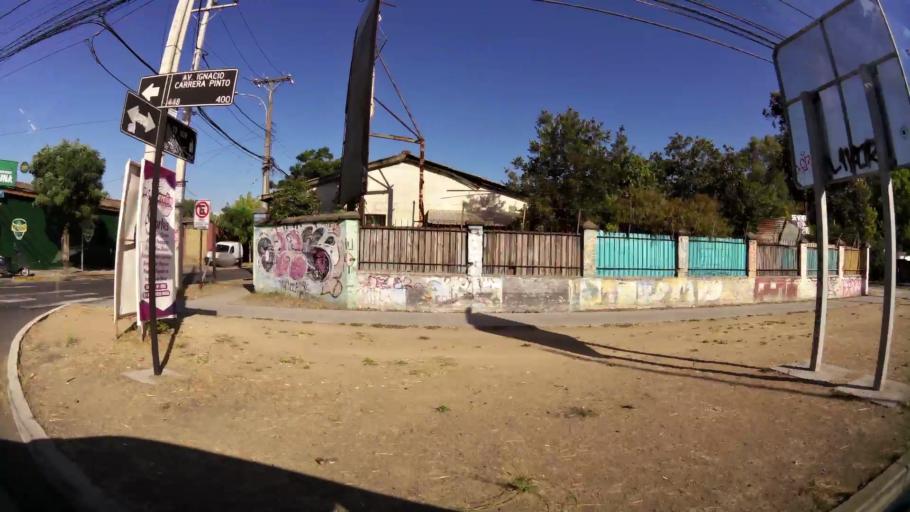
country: CL
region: Maule
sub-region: Provincia de Talca
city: Talca
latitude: -35.4320
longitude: -71.6776
